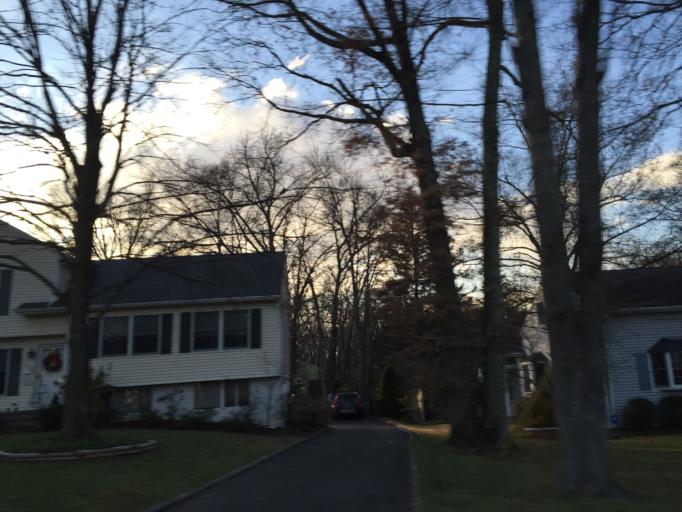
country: US
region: New Jersey
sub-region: Union County
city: Summit
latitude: 40.7310
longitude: -74.3684
